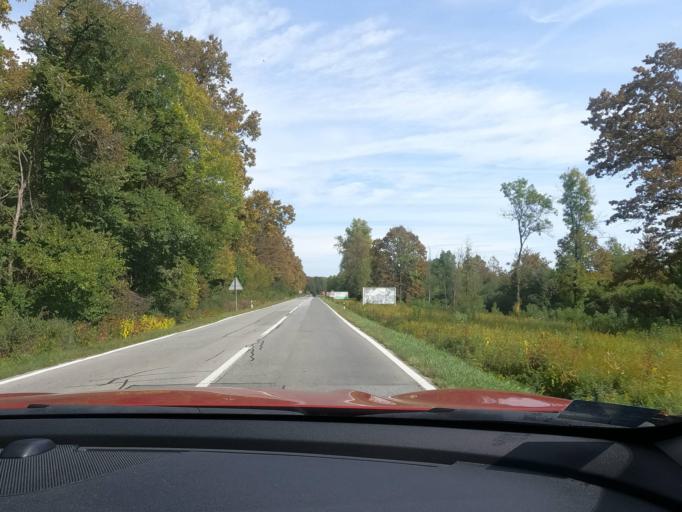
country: HR
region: Sisacko-Moslavacka
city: Budasevo
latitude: 45.4879
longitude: 16.4838
